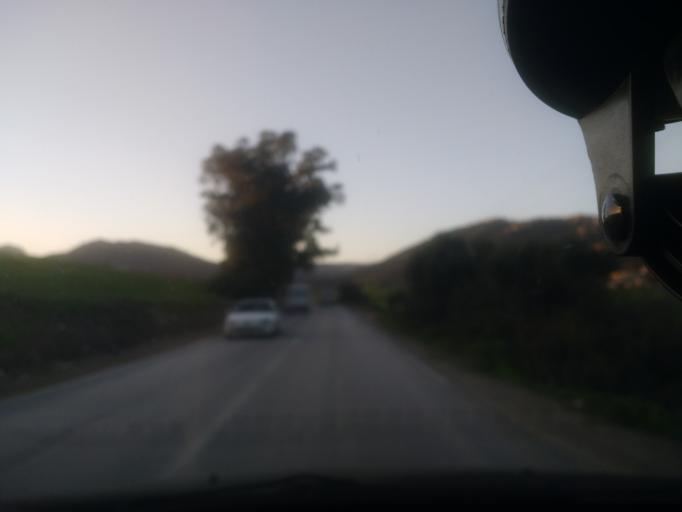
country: DZ
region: Boumerdes
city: Makouda
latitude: 36.7698
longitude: 4.0650
